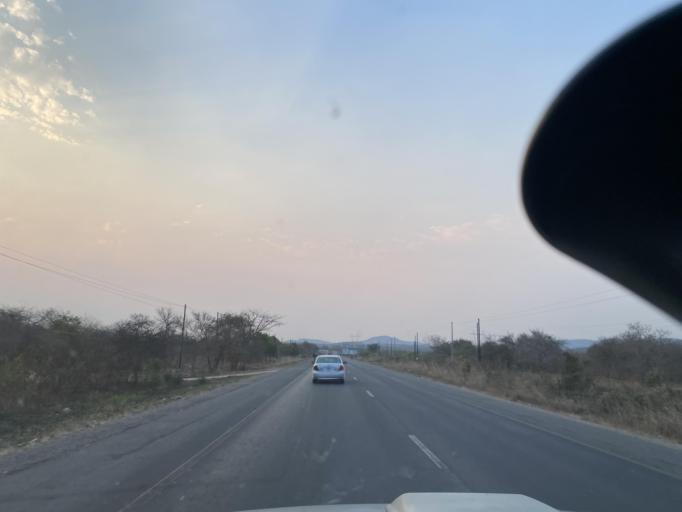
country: ZM
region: Lusaka
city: Kafue
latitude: -15.8286
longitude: 28.2320
